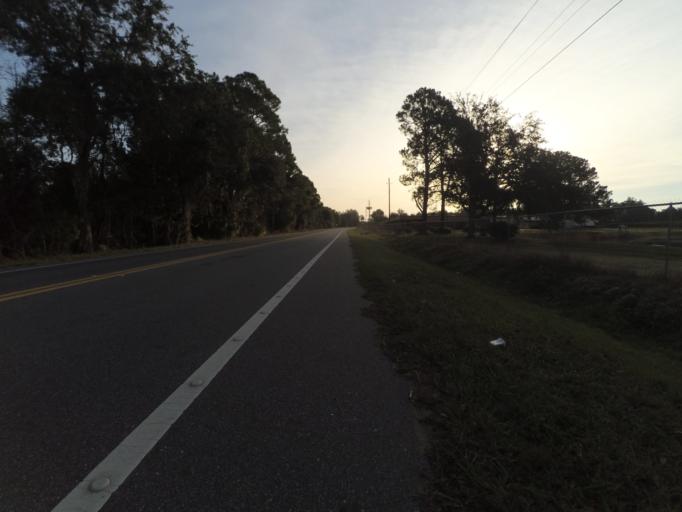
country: US
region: Florida
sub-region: Lake County
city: Umatilla
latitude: 28.9305
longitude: -81.6952
